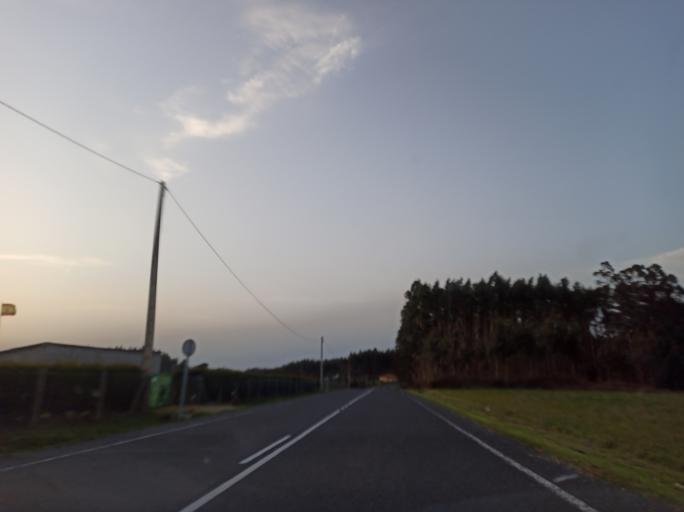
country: ES
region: Galicia
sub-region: Provincia da Coruna
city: Coiros
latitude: 43.1784
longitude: -8.1192
